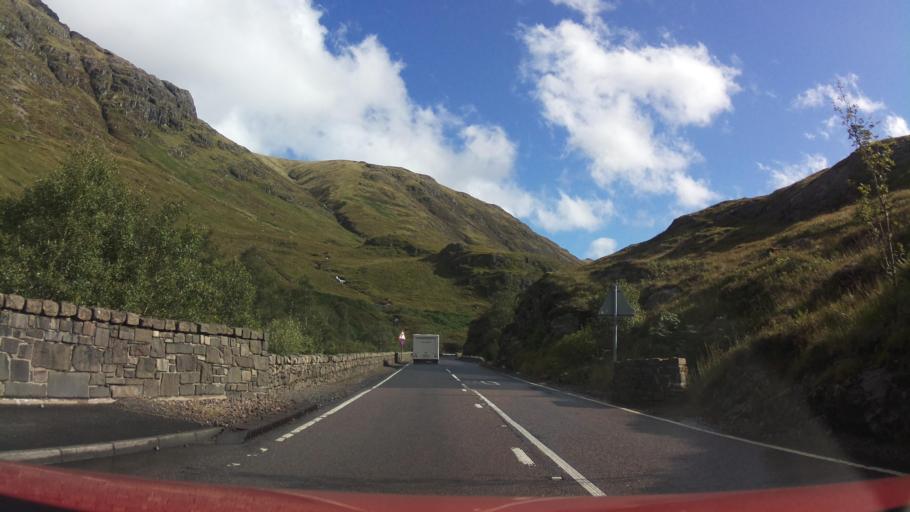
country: GB
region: Scotland
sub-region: Highland
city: Fort William
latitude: 56.6625
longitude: -4.9639
